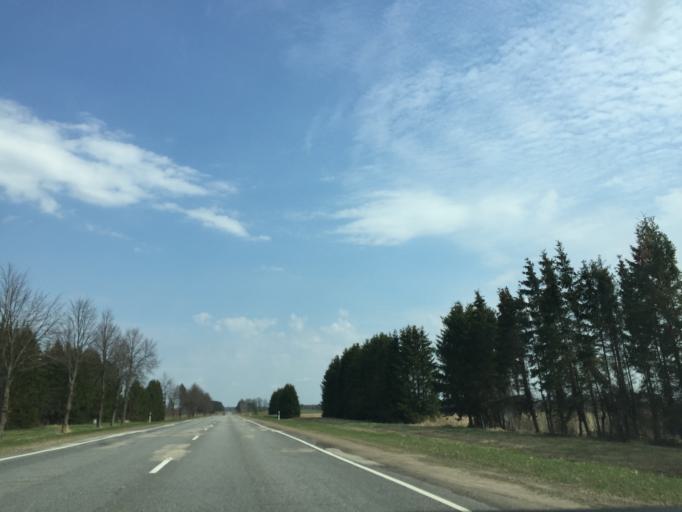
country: LV
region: Apes Novads
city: Ape
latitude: 57.4633
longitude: 26.4128
